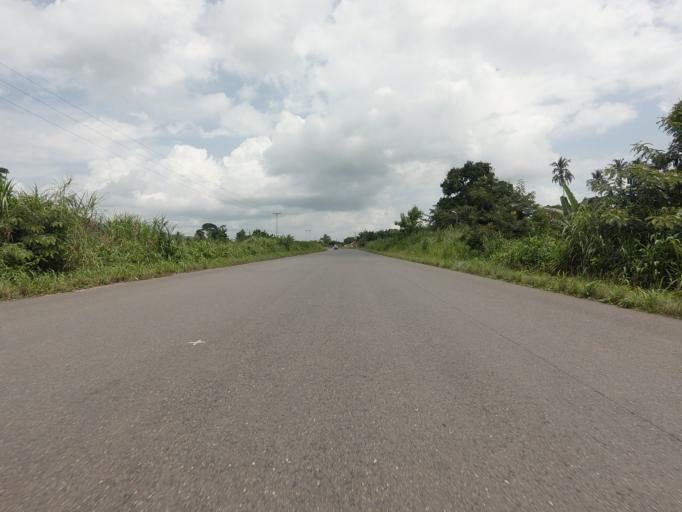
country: GH
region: Volta
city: Ho
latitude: 6.5031
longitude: 0.2073
